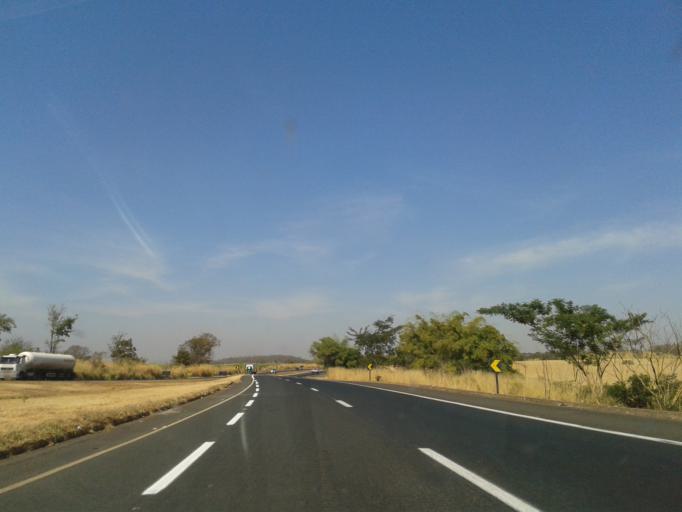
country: BR
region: Goias
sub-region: Goiatuba
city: Goiatuba
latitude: -18.0842
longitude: -49.2709
